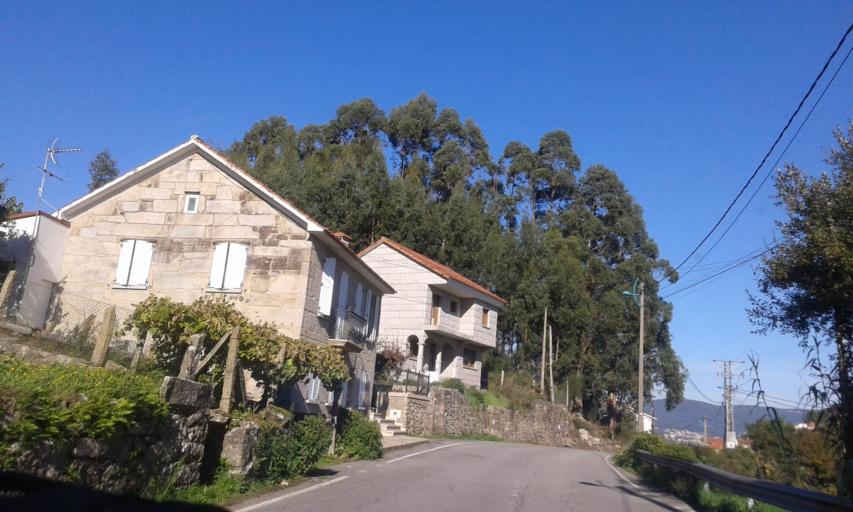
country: ES
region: Galicia
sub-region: Provincia de Pontevedra
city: Marin
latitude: 42.3659
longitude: -8.7390
